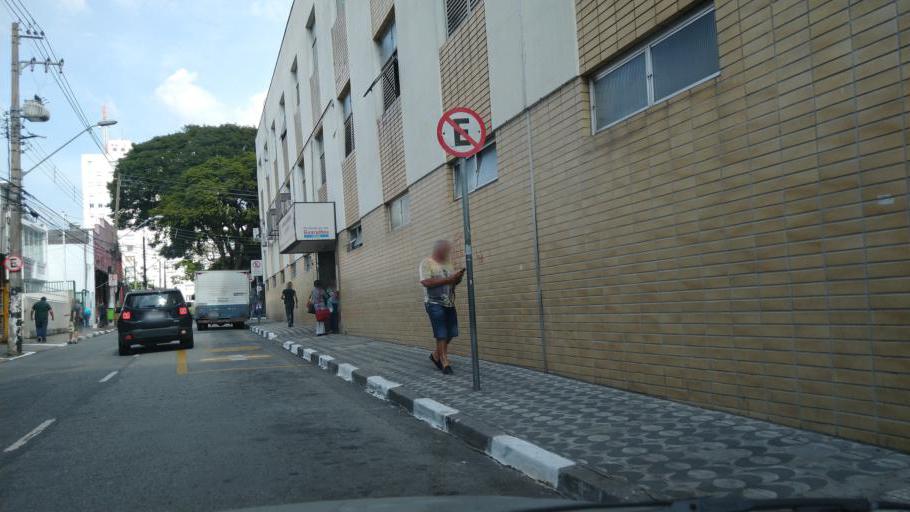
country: BR
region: Sao Paulo
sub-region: Guarulhos
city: Guarulhos
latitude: -23.4674
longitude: -46.5321
